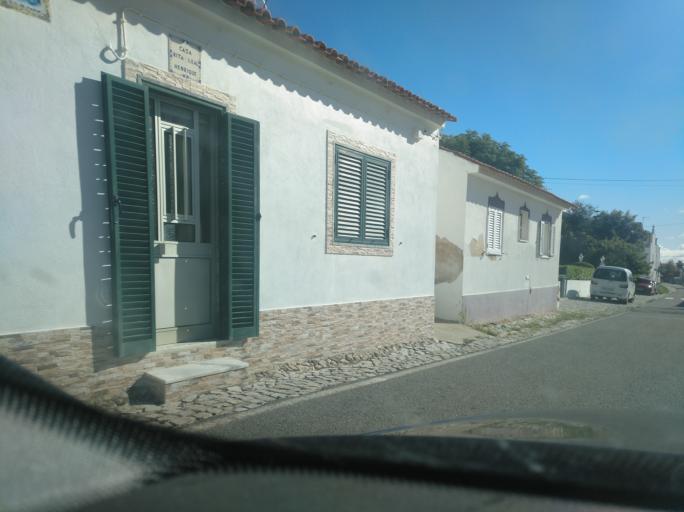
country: PT
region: Faro
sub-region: Vila Real de Santo Antonio
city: Monte Gordo
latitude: 37.1709
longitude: -7.5254
